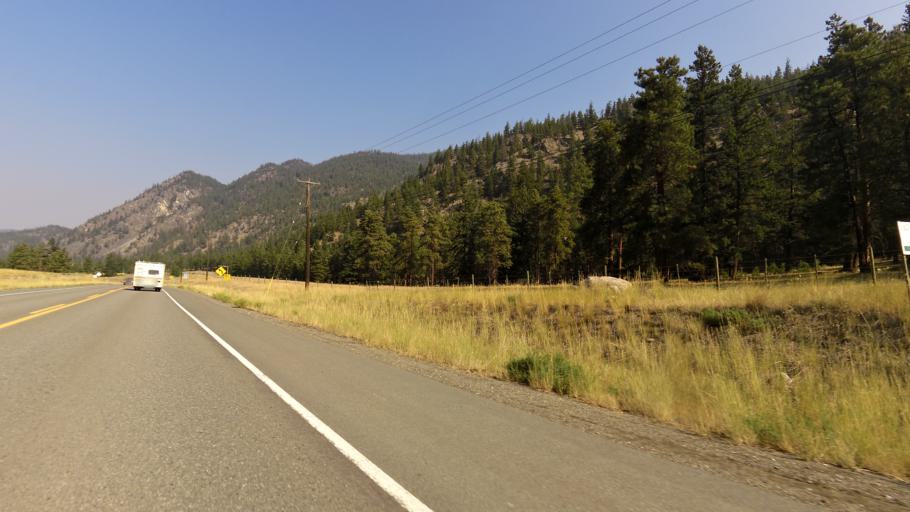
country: CA
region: British Columbia
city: Princeton
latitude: 49.3761
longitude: -120.1463
